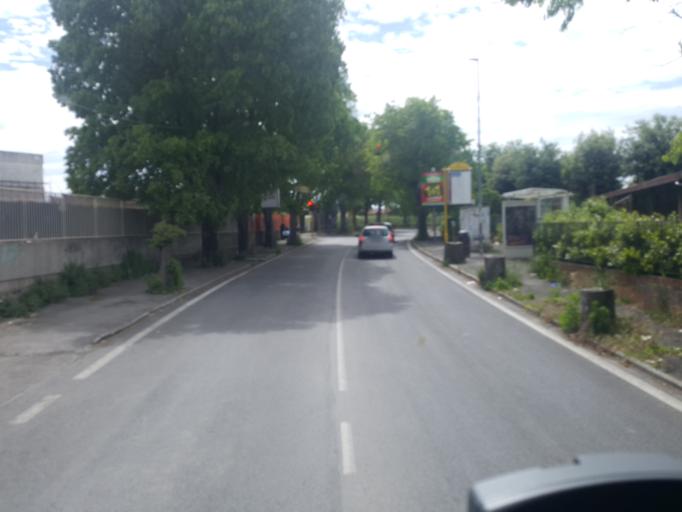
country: IT
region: Latium
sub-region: Citta metropolitana di Roma Capitale
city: La Massimina-Casal Lumbroso
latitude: 41.8816
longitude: 12.3513
